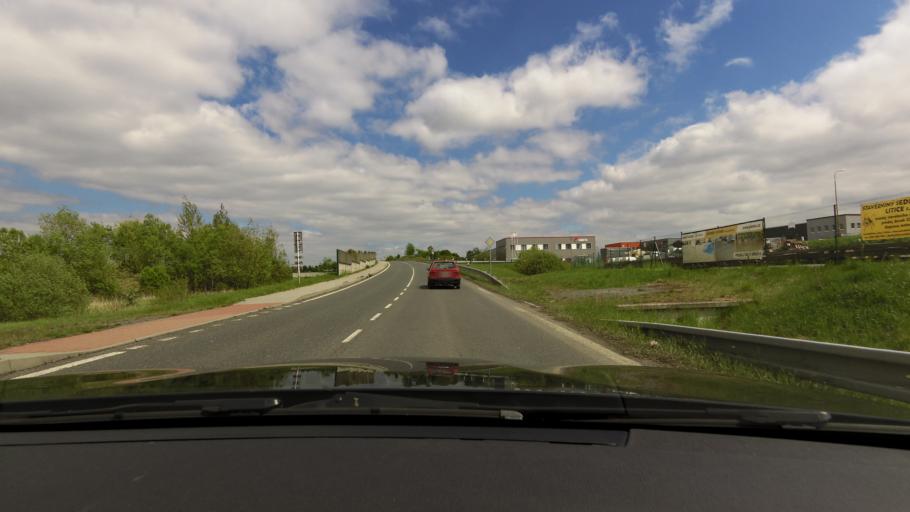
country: CZ
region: Plzensky
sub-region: Okres Plzen-Mesto
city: Pilsen
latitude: 49.7093
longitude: 13.3579
